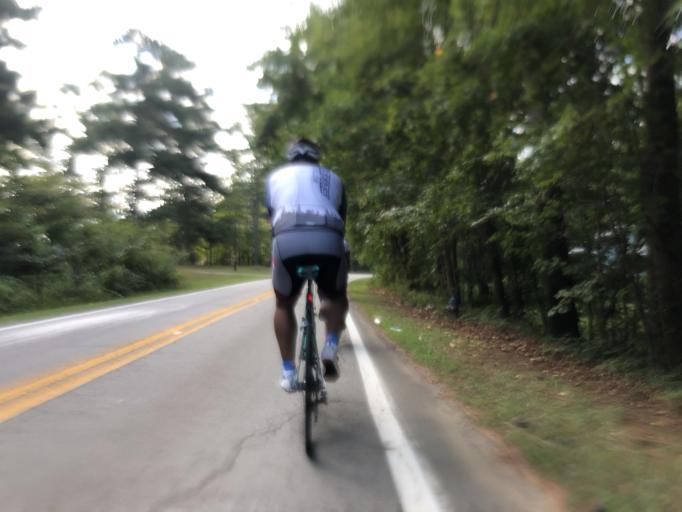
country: US
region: Georgia
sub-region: Fulton County
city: Palmetto
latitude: 33.5827
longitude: -84.6507
